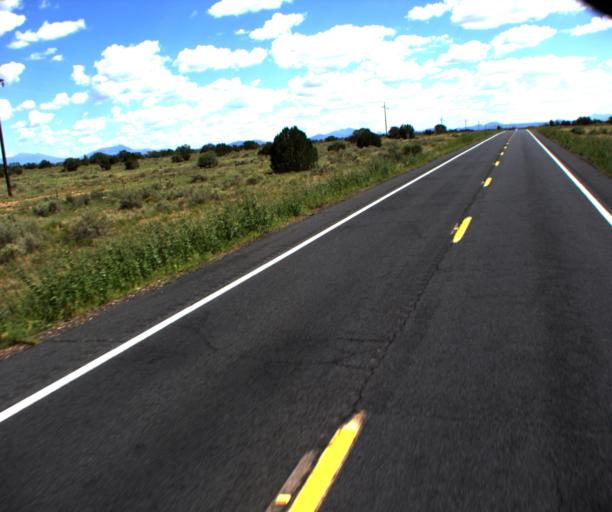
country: US
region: Arizona
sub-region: Coconino County
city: Grand Canyon Village
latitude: 35.7262
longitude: -112.1312
